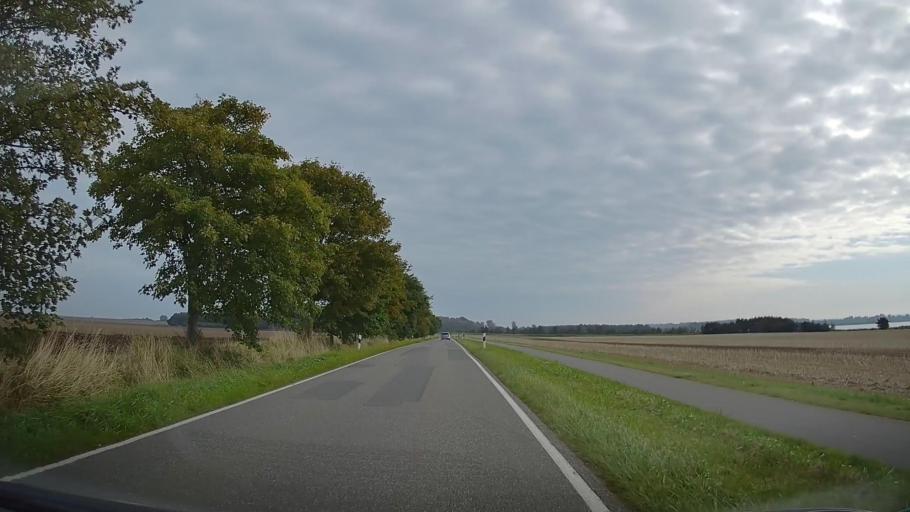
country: DE
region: Schleswig-Holstein
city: Panker
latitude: 54.3390
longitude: 10.6229
